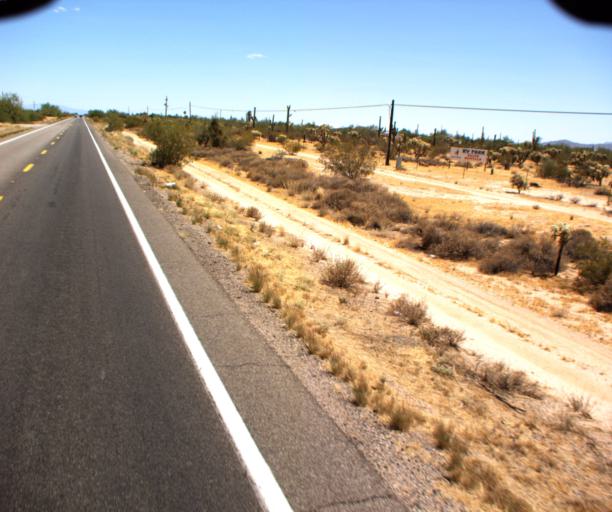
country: US
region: Arizona
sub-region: Pinal County
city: Florence
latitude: 32.9679
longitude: -111.3426
